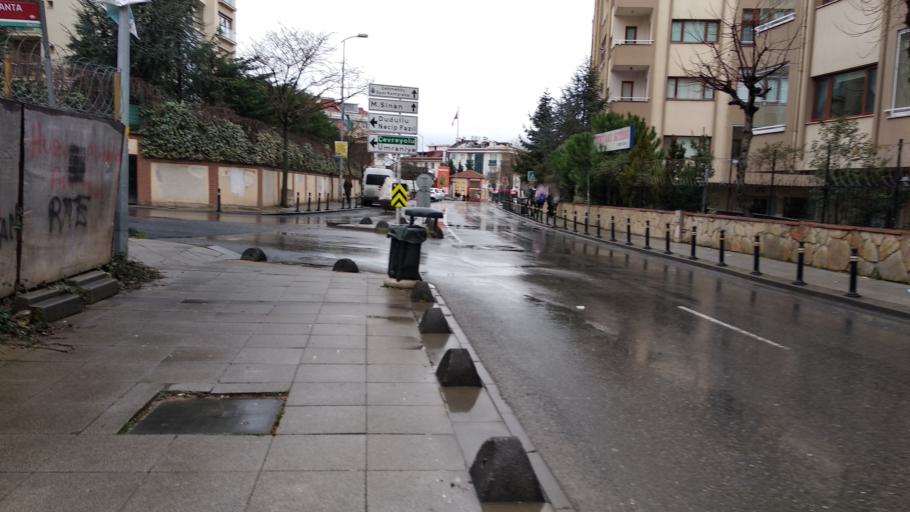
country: TR
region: Istanbul
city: Samandira
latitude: 41.0224
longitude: 29.1858
